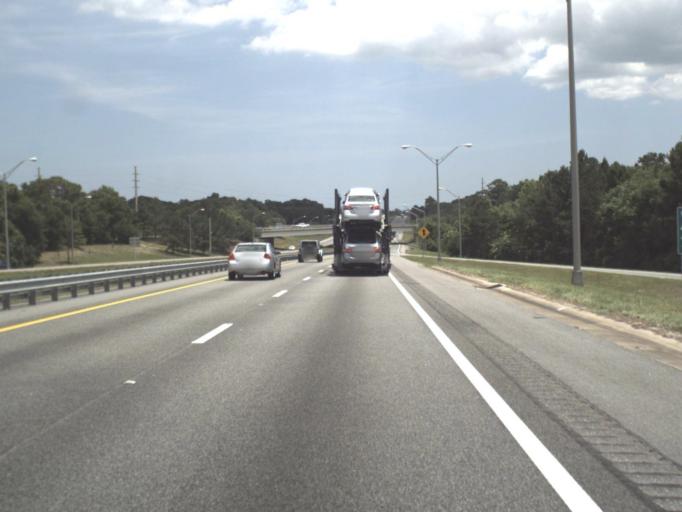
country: US
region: Florida
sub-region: Duval County
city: Jacksonville
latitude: 30.3395
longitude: -81.5405
